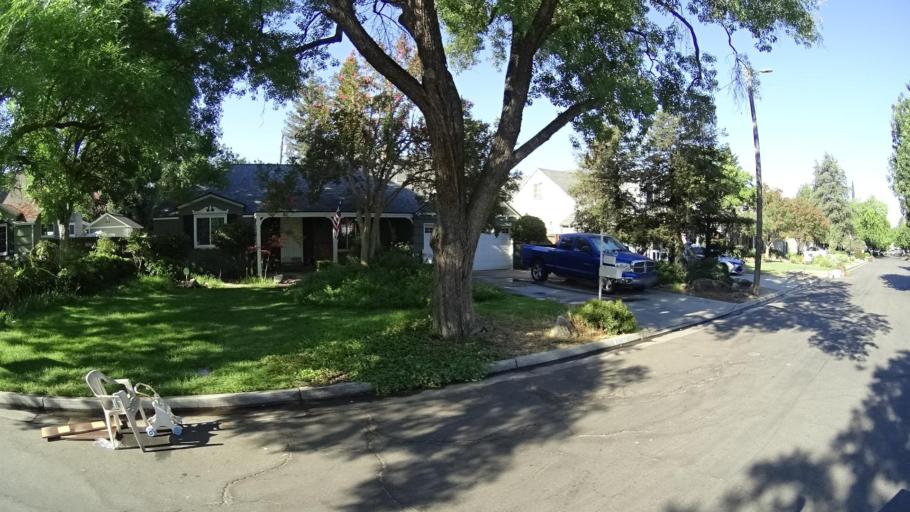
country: US
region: California
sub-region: Fresno County
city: Fresno
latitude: 36.7912
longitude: -119.7689
